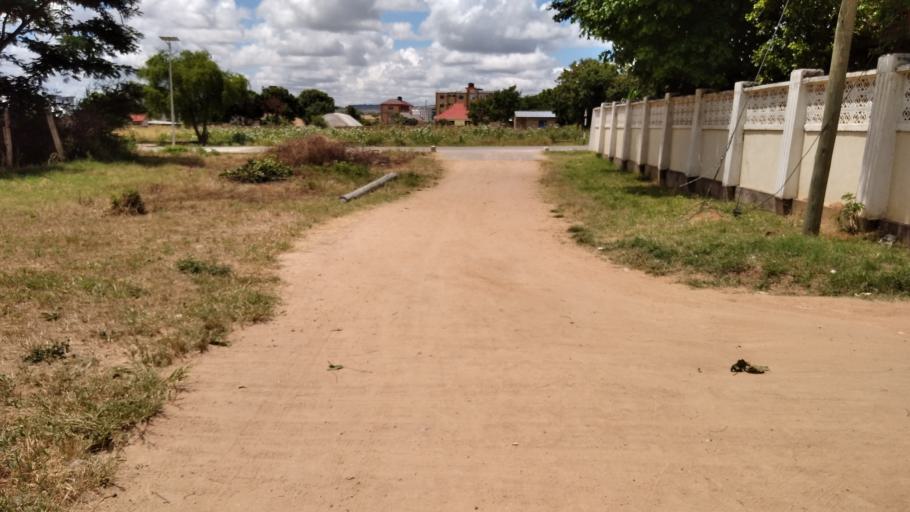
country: TZ
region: Dodoma
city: Dodoma
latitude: -6.1899
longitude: 35.7534
